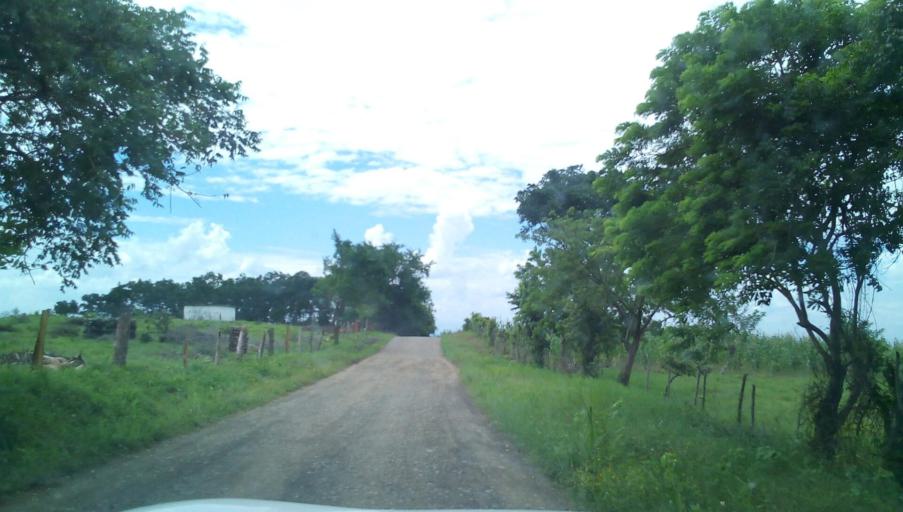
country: MX
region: Veracruz
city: Tepetzintla
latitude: 21.1312
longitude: -97.8522
